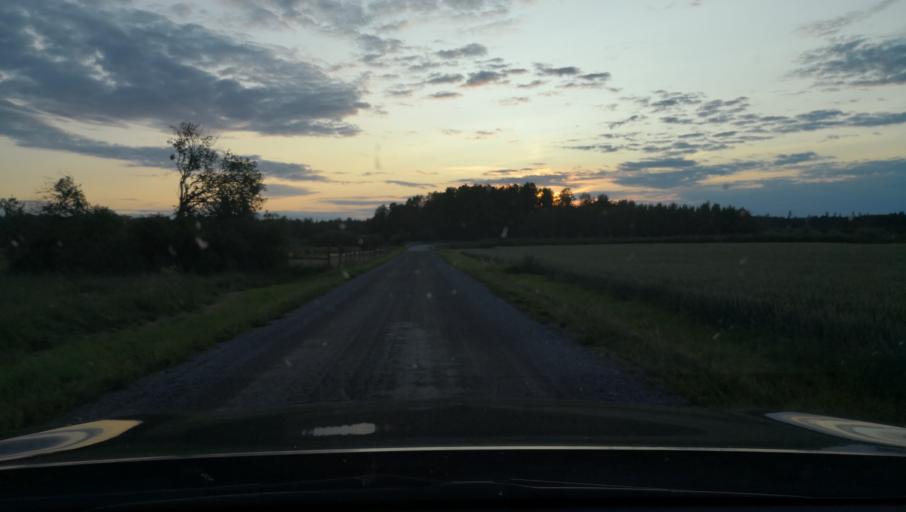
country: SE
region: Uppsala
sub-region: Osthammars Kommun
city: Bjorklinge
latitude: 60.0598
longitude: 17.5839
